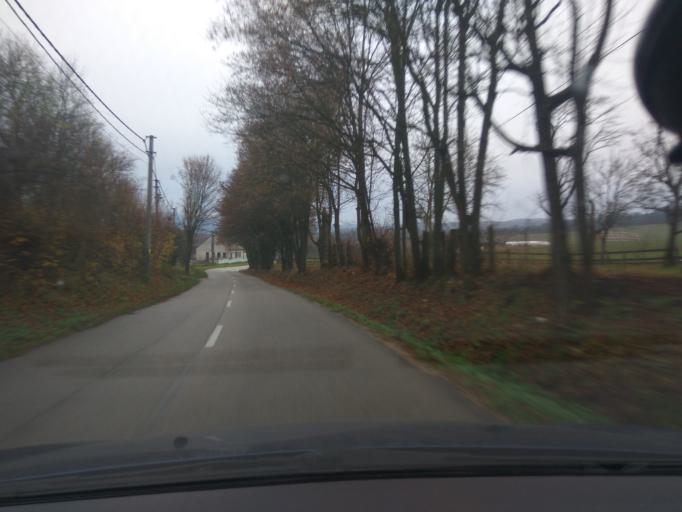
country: SK
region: Trnavsky
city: Vrbove
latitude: 48.6819
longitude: 17.6686
